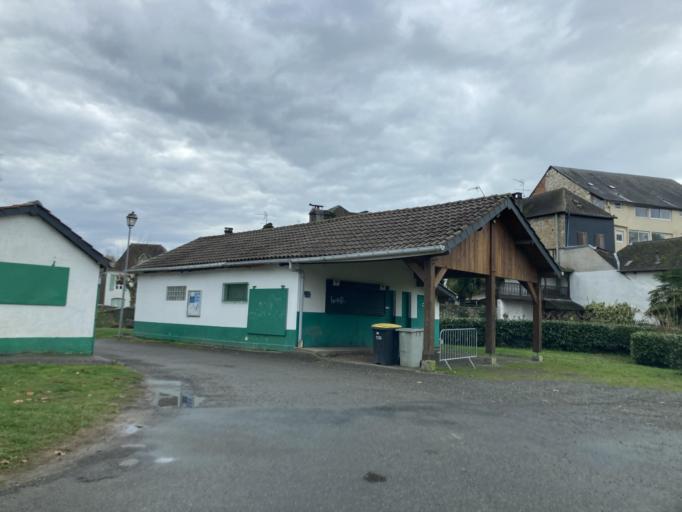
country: FR
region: Aquitaine
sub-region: Departement des Pyrenees-Atlantiques
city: Lasseube
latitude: 43.2213
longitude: -0.4767
